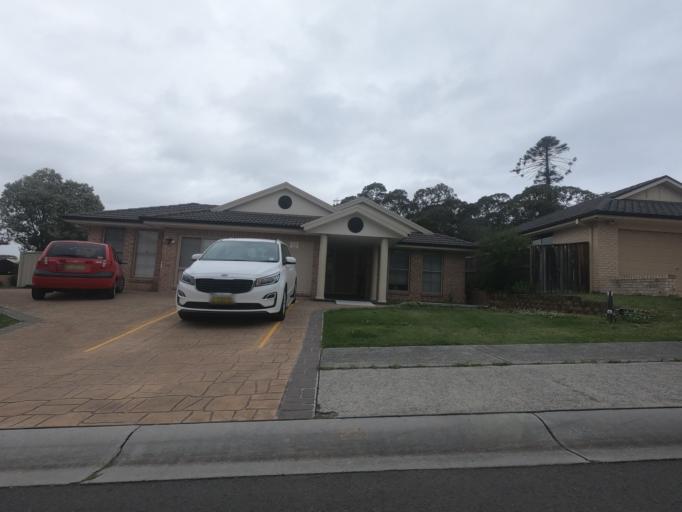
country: AU
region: New South Wales
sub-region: Wollongong
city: Dapto
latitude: -34.4845
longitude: 150.7785
